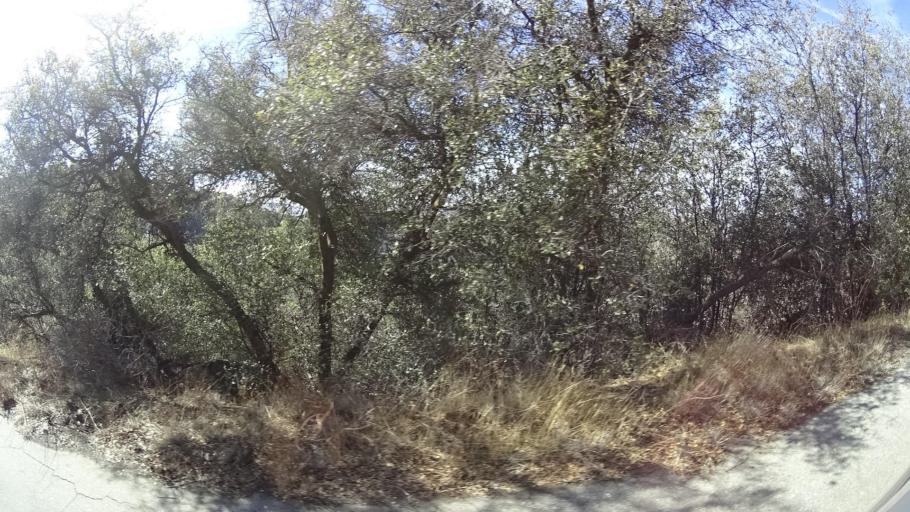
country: US
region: California
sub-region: Kern County
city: Bodfish
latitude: 35.4670
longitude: -118.6493
